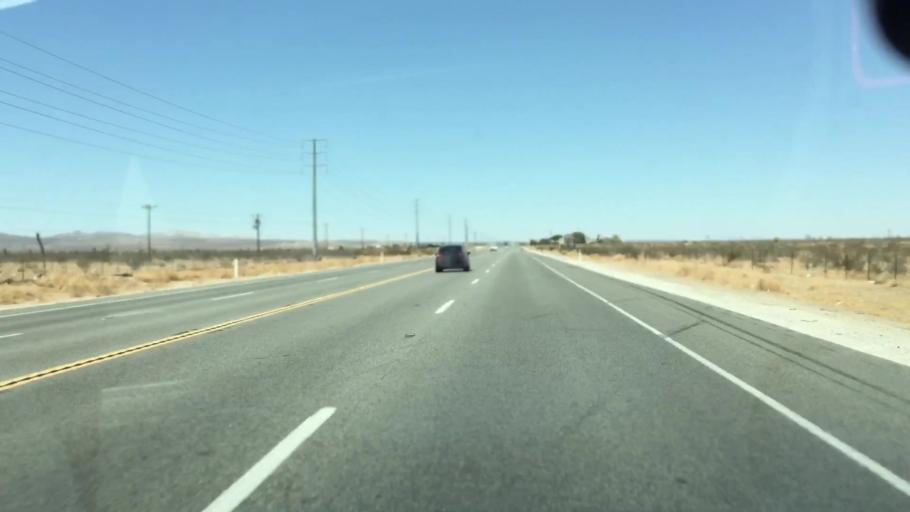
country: US
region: California
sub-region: San Bernardino County
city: Adelanto
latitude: 34.5946
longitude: -117.4172
